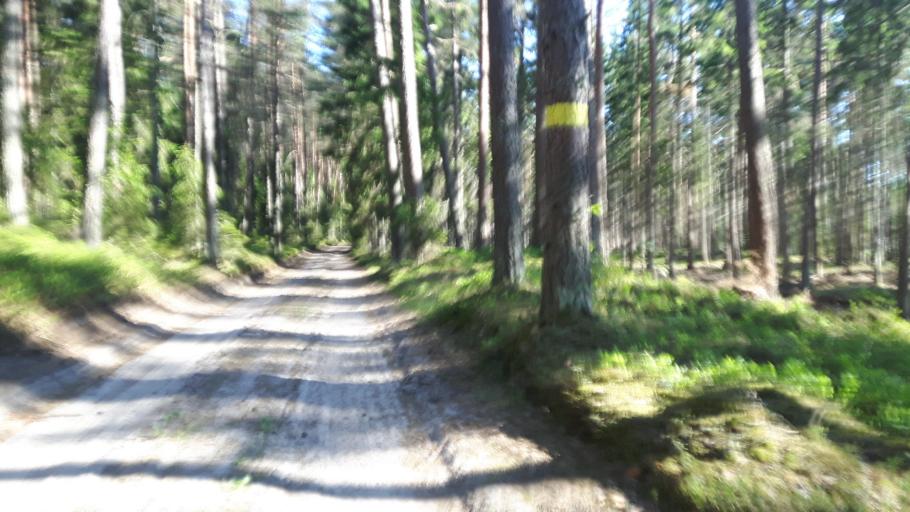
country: LV
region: Salacgrivas
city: Salacgriva
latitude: 57.7158
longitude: 24.3488
